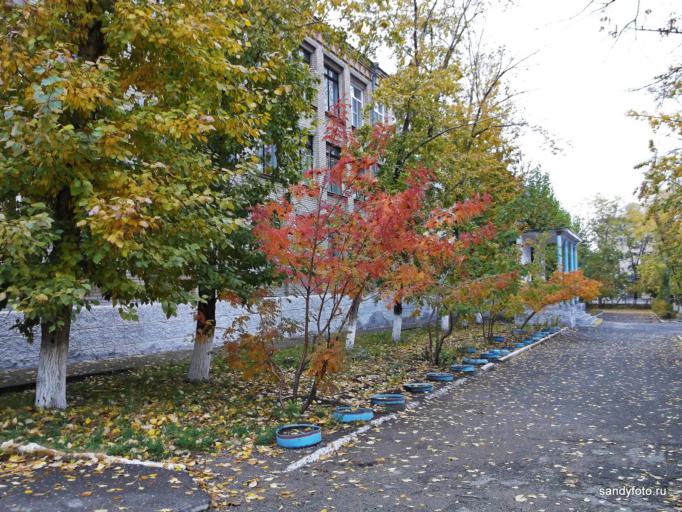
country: RU
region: Chelyabinsk
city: Troitsk
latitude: 54.0792
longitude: 61.5356
